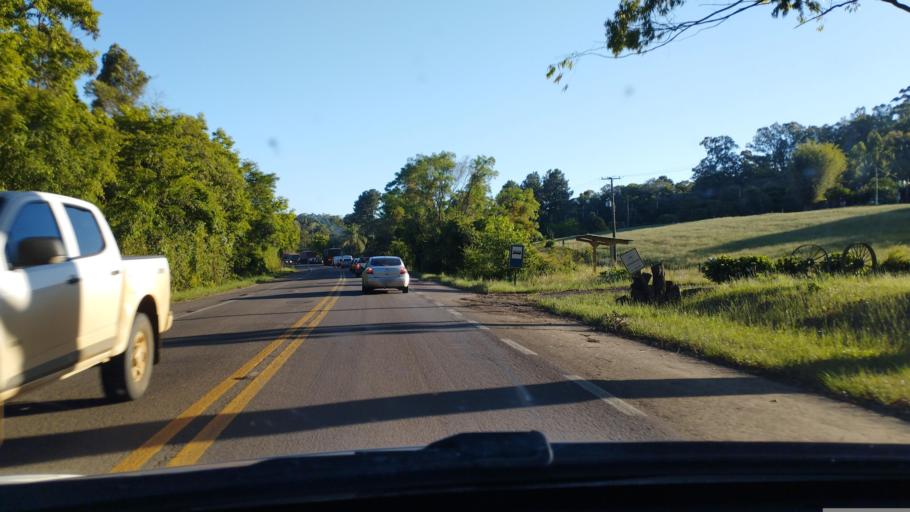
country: BR
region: Rio Grande do Sul
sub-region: Santa Maria
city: Santa Maria
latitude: -29.5978
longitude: -53.7674
